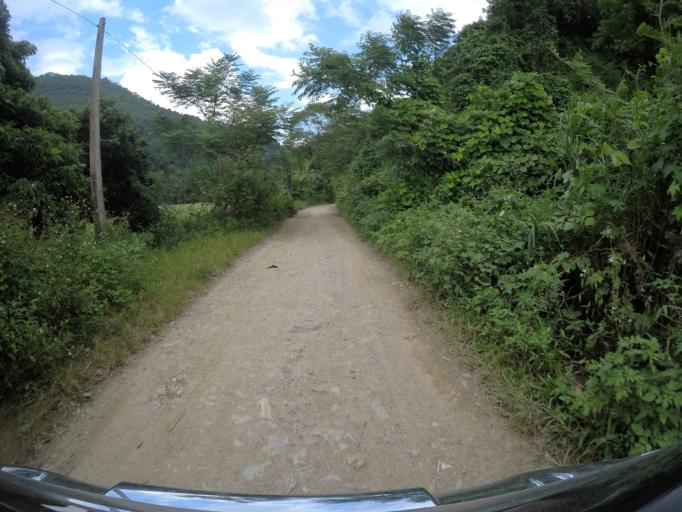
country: VN
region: Yen Bai
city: Son Thinh
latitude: 21.6662
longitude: 104.5134
